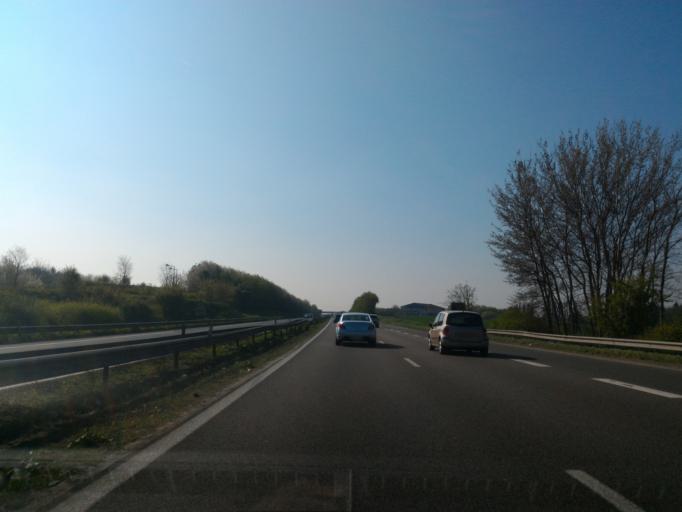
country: FR
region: Ile-de-France
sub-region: Departement de Seine-et-Marne
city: Servon
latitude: 48.6991
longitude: 2.5940
